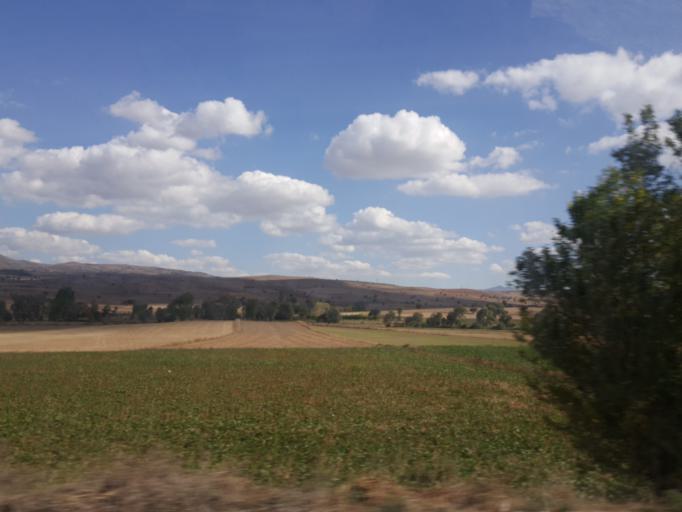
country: TR
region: Tokat
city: Camlibel
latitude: 40.1827
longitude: 36.4502
